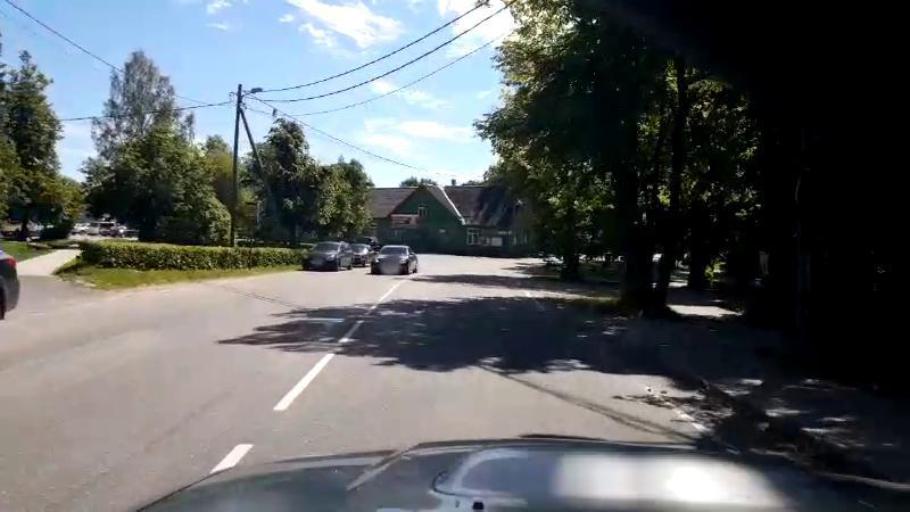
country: EE
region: Jaervamaa
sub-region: Jaerva-Jaani vald
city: Jarva-Jaani
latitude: 59.0398
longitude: 25.8807
